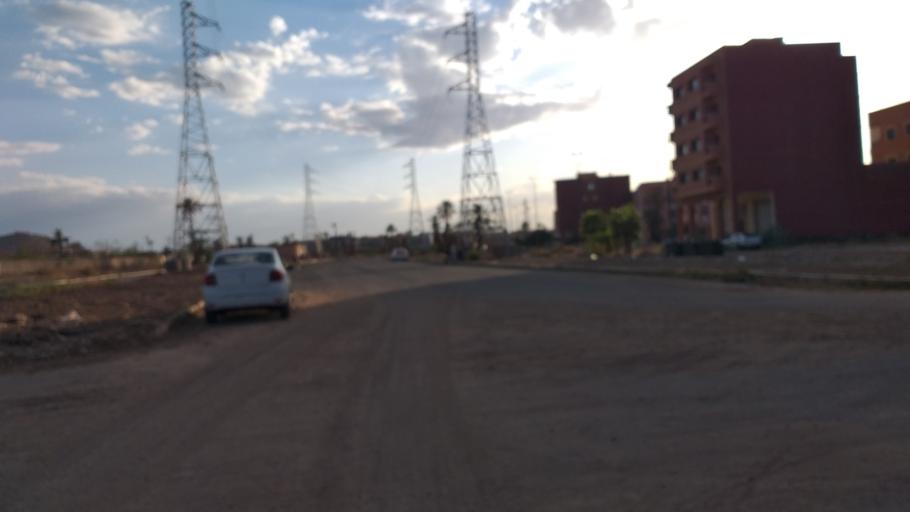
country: MA
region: Marrakech-Tensift-Al Haouz
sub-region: Marrakech
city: Marrakesh
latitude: 31.6670
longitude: -8.0217
